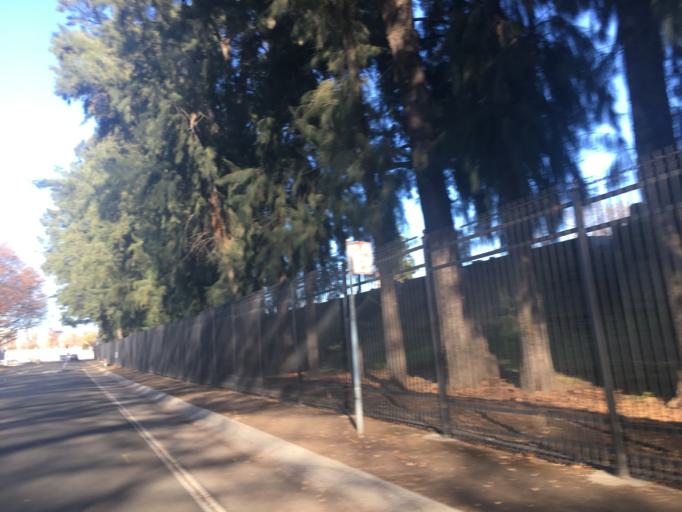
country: US
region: California
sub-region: Sacramento County
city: Sacramento
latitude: 38.5630
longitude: -121.5030
